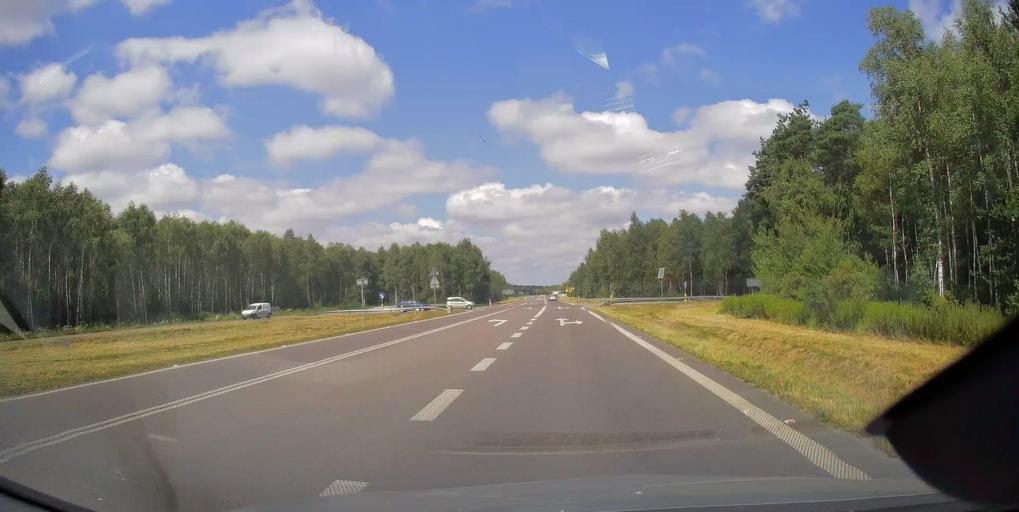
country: PL
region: Subcarpathian Voivodeship
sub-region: Powiat mielecki
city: Mielec
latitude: 50.3236
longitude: 21.4928
